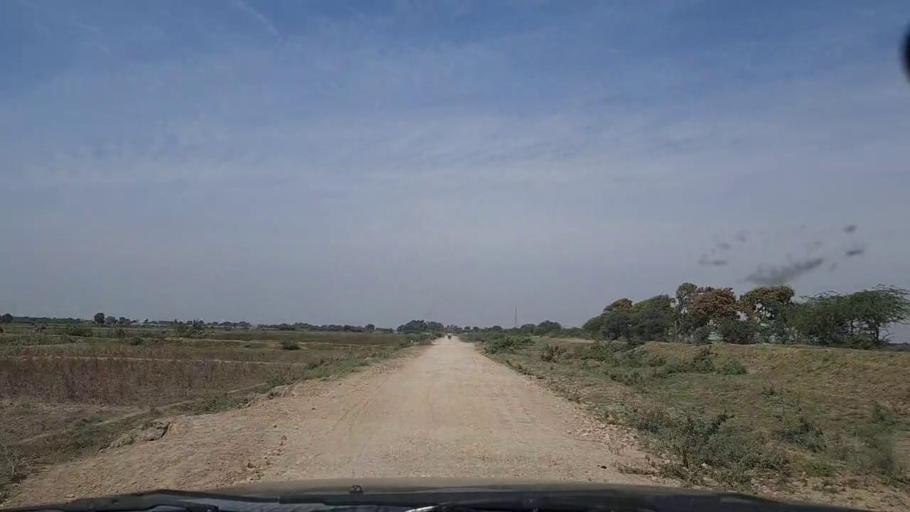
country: PK
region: Sindh
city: Mirpur Batoro
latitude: 24.6494
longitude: 68.1850
